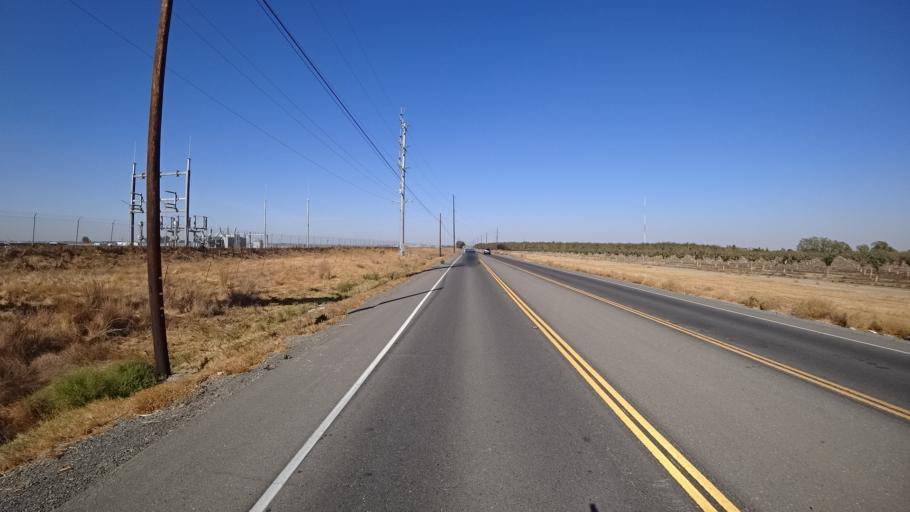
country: US
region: California
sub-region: Yolo County
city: Davis
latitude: 38.5809
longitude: -121.7306
